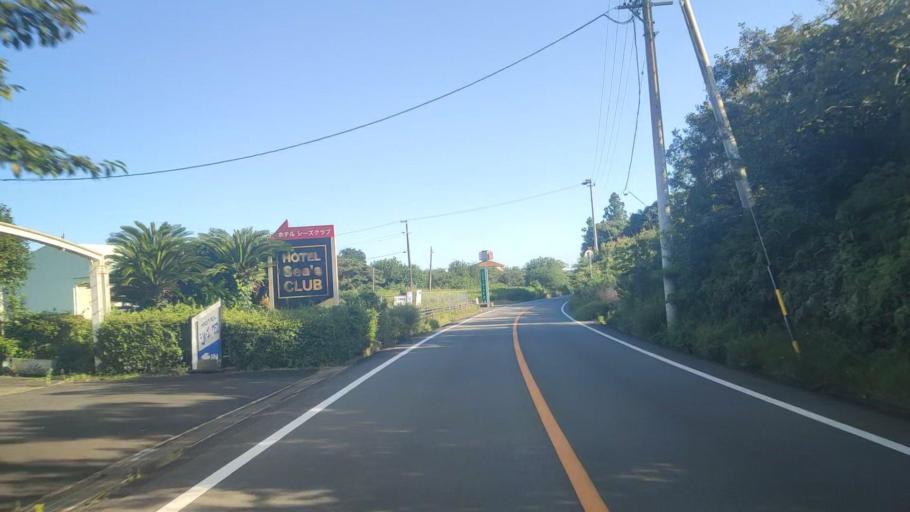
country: JP
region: Mie
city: Toba
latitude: 34.3408
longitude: 136.8401
